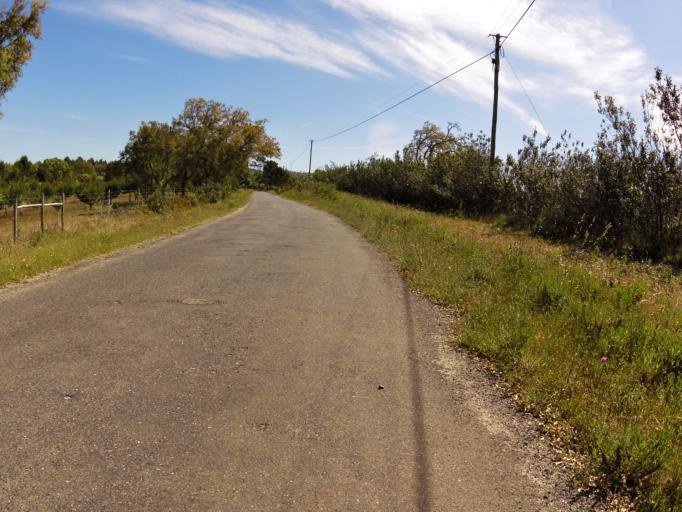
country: PT
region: Setubal
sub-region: Santiago do Cacem
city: Santiago do Cacem
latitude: 37.9398
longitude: -8.7379
